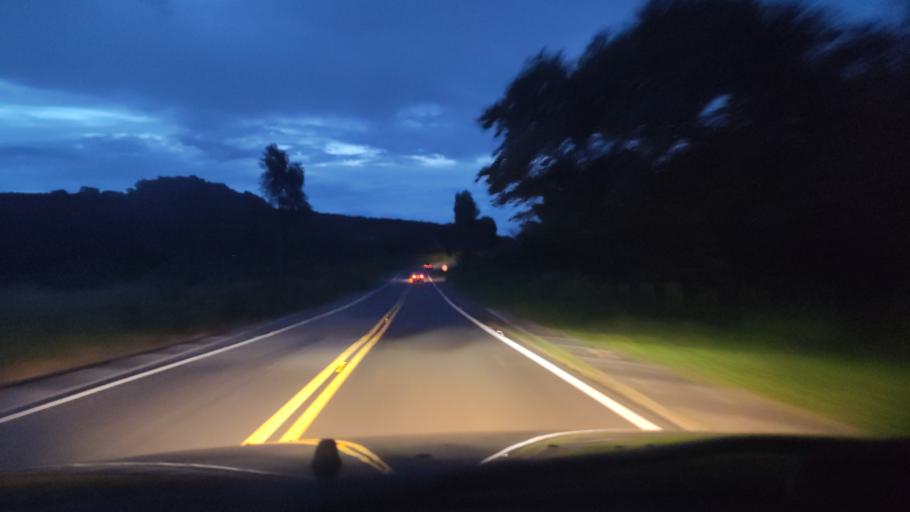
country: BR
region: Sao Paulo
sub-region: Socorro
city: Socorro
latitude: -22.5599
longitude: -46.5953
